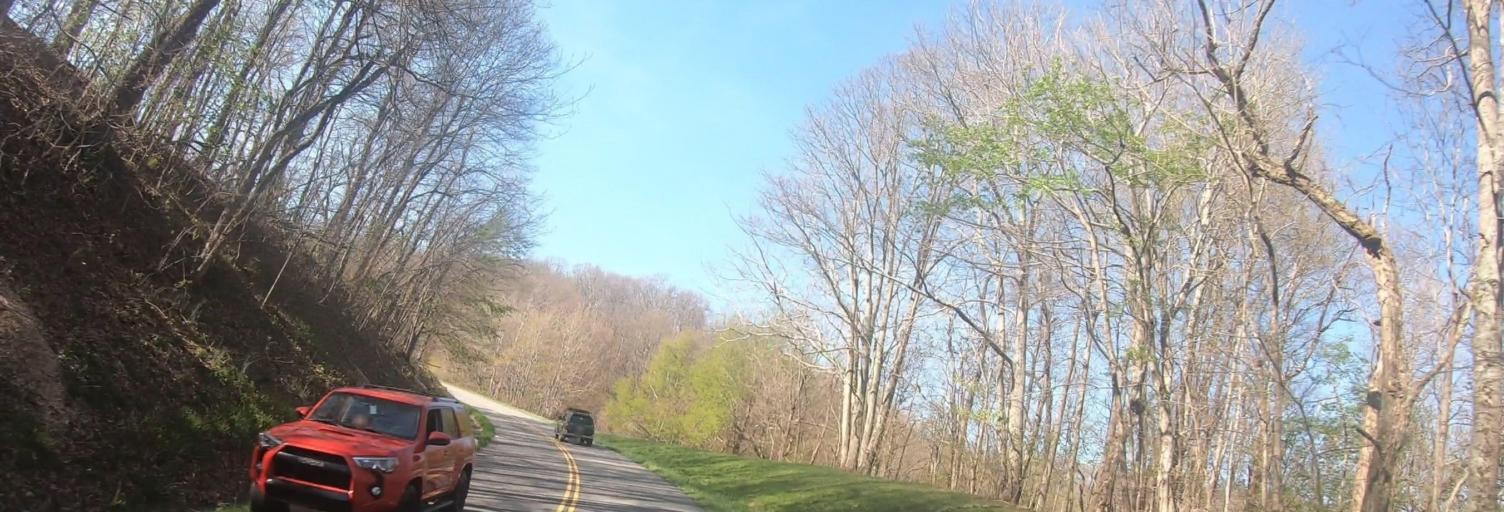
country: US
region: North Carolina
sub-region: Watauga County
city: Boone
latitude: 36.2054
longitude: -81.6018
